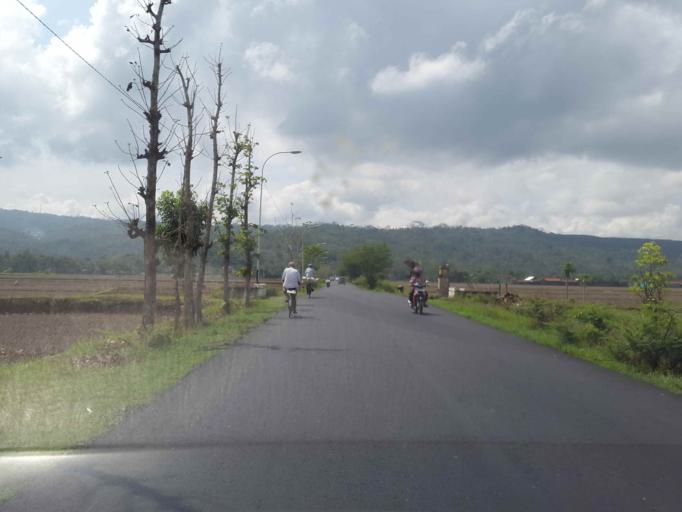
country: ID
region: Central Java
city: Banyumas
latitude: -7.5213
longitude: 109.3026
